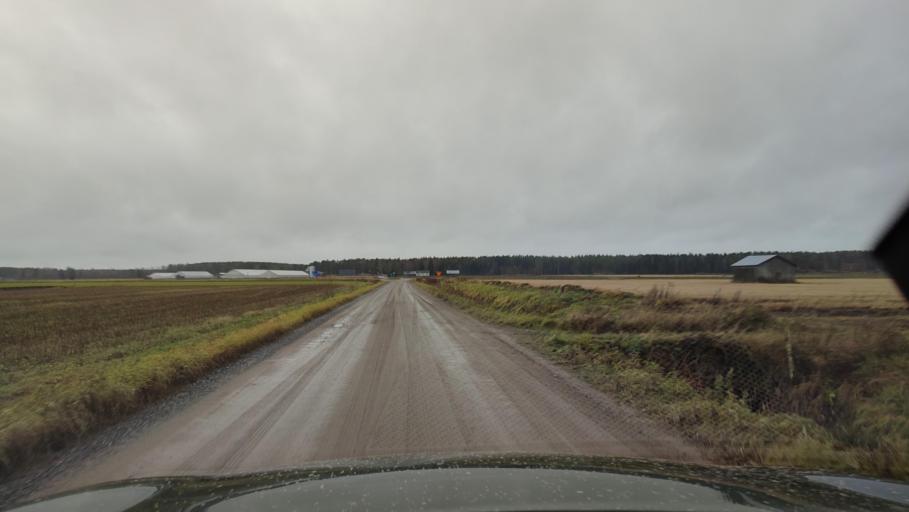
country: FI
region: Ostrobothnia
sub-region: Sydosterbotten
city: Naerpes
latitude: 62.4468
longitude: 21.4325
